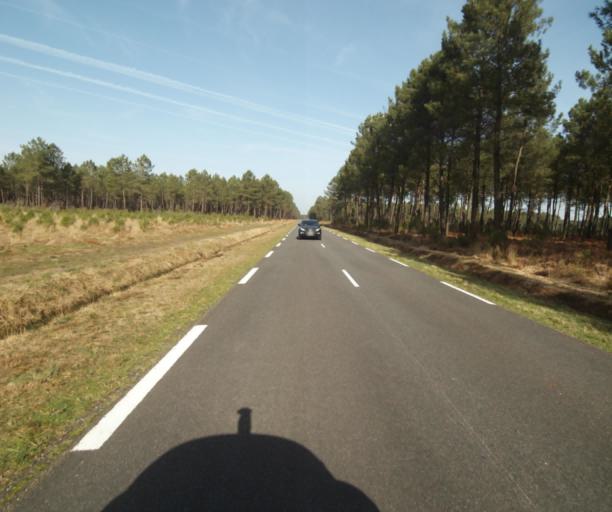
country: FR
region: Aquitaine
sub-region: Departement du Lot-et-Garonne
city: Casteljaloux
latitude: 44.1637
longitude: 0.0634
